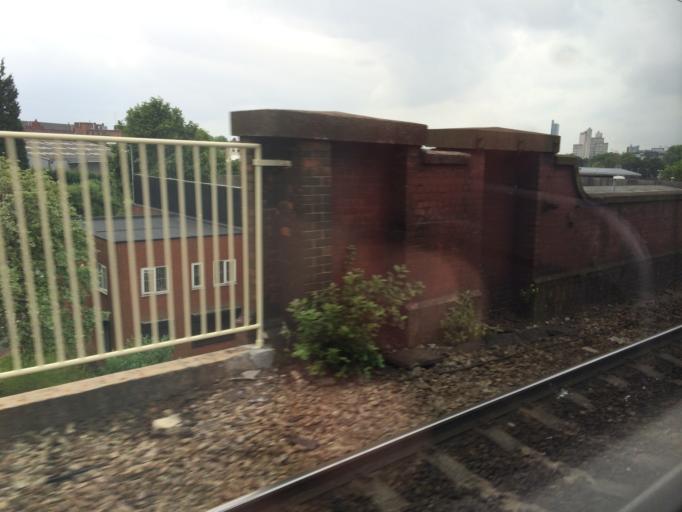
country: GB
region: England
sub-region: Manchester
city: Longsight
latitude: 53.4723
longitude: -2.2164
